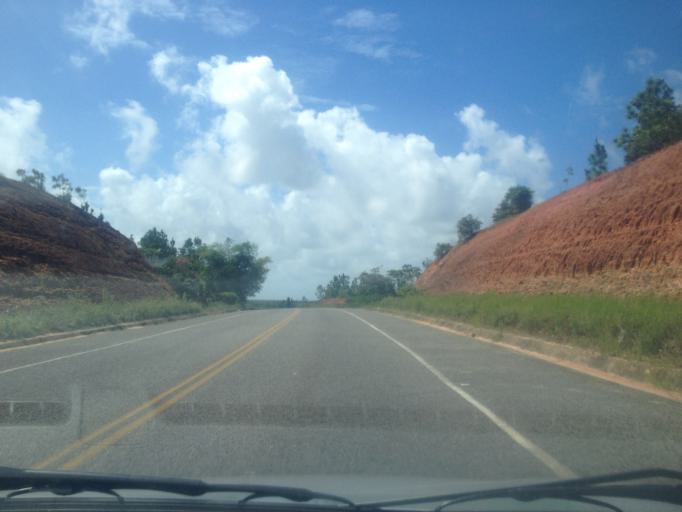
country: BR
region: Bahia
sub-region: Conde
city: Conde
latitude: -11.8798
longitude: -37.6464
